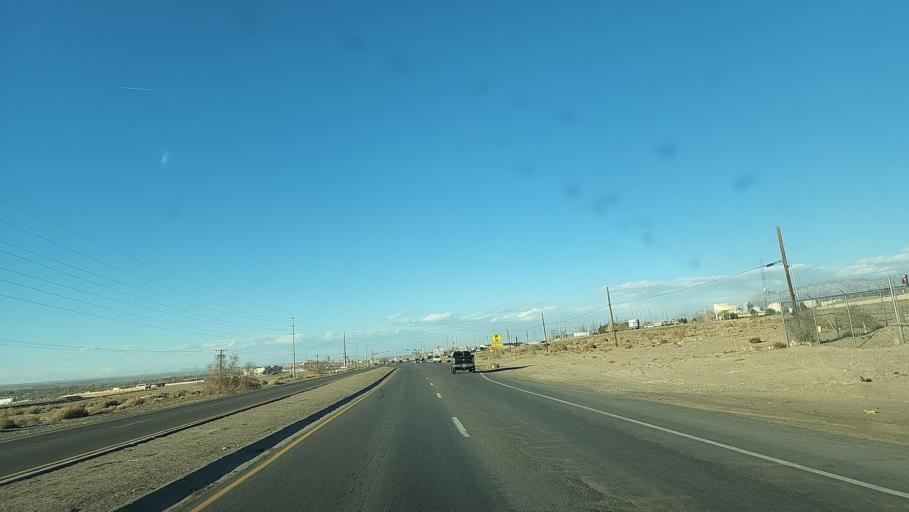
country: US
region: New Mexico
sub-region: Bernalillo County
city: South Valley
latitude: 35.0220
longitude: -106.6468
